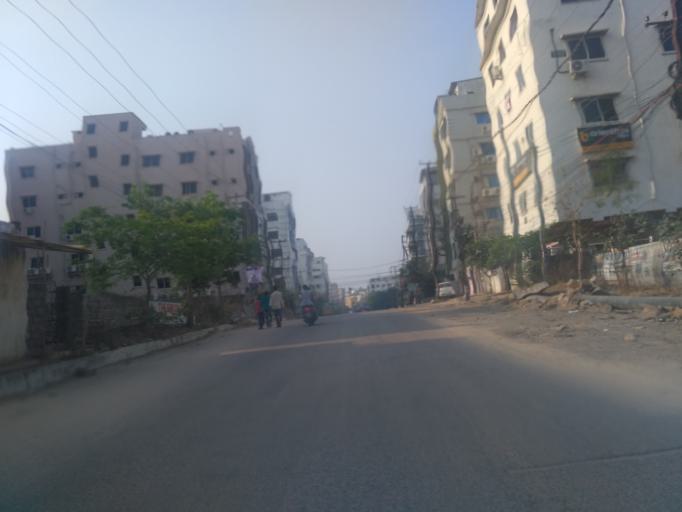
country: IN
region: Telangana
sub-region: Rangareddi
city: Kukatpalli
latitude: 17.4494
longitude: 78.3919
